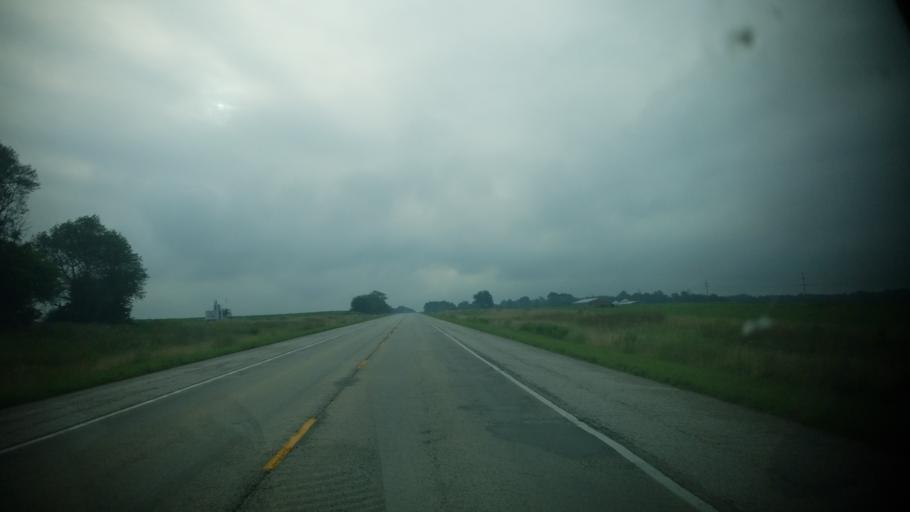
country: US
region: Illinois
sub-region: Clay County
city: Flora
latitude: 38.6772
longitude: -88.4127
